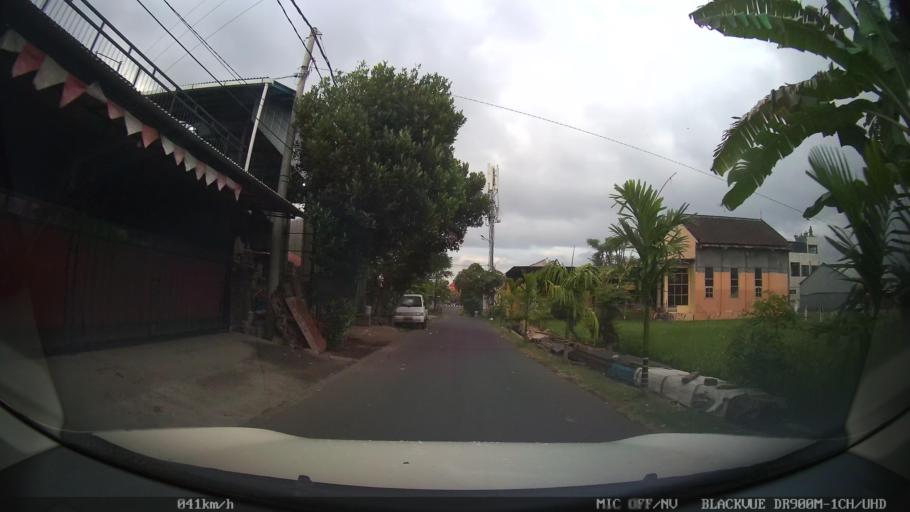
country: ID
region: Bali
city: Banjar Pasekan
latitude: -8.6419
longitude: 115.2795
